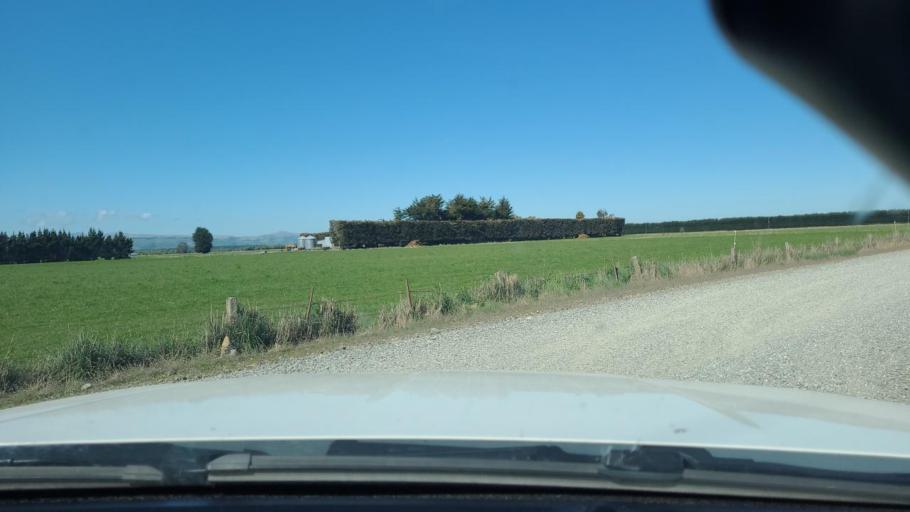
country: NZ
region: Southland
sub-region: Gore District
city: Gore
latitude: -45.8252
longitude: 168.6541
